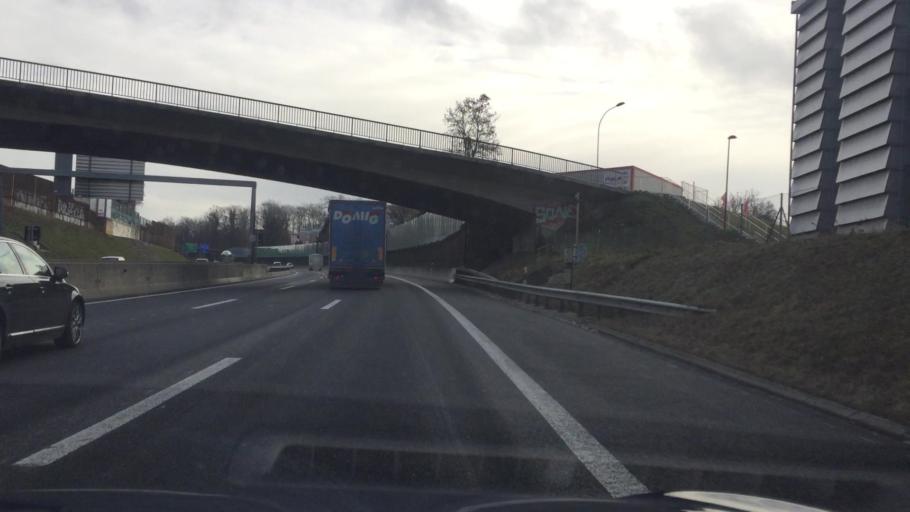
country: CH
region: Vaud
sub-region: Lausanne District
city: Blecherette
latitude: 46.5439
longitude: 6.6337
